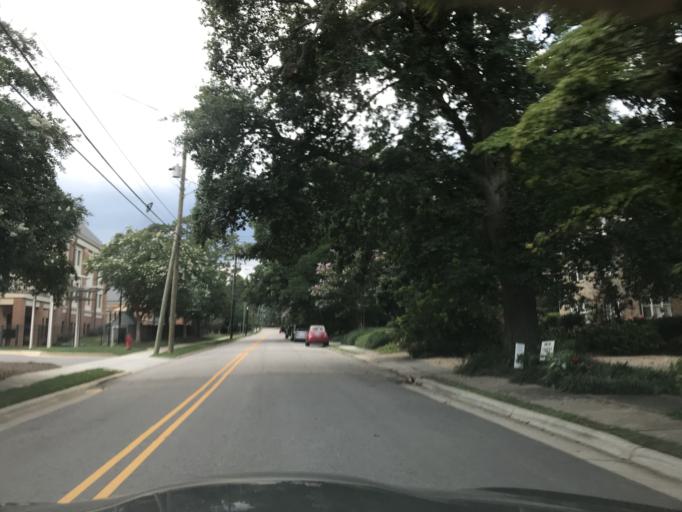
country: US
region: North Carolina
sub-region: Wake County
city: West Raleigh
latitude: 35.8067
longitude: -78.6501
